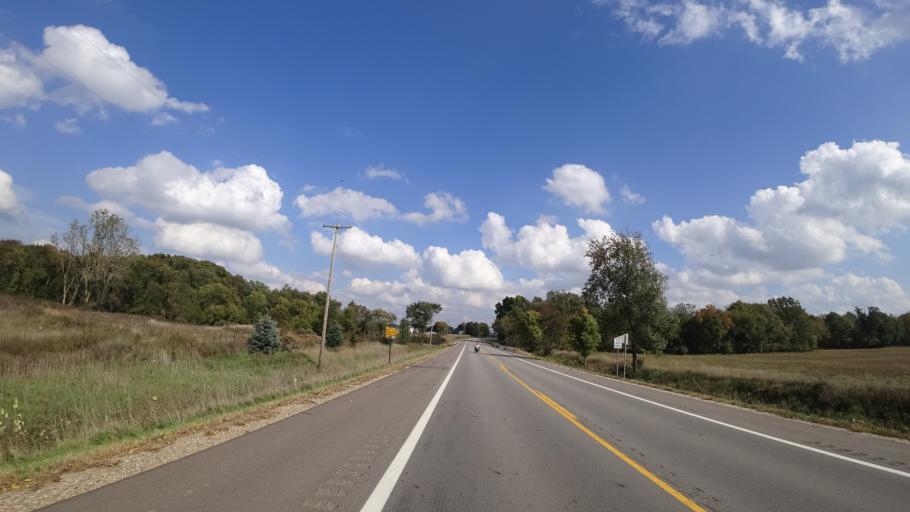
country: US
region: Michigan
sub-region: Calhoun County
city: Athens
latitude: 42.0612
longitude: -85.2572
